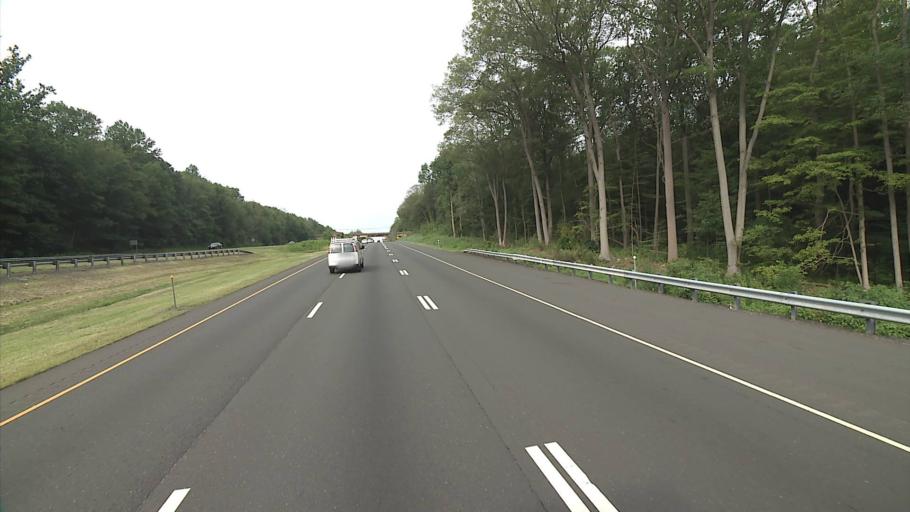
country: US
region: Connecticut
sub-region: New Haven County
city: Southbury
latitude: 41.4908
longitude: -73.1703
